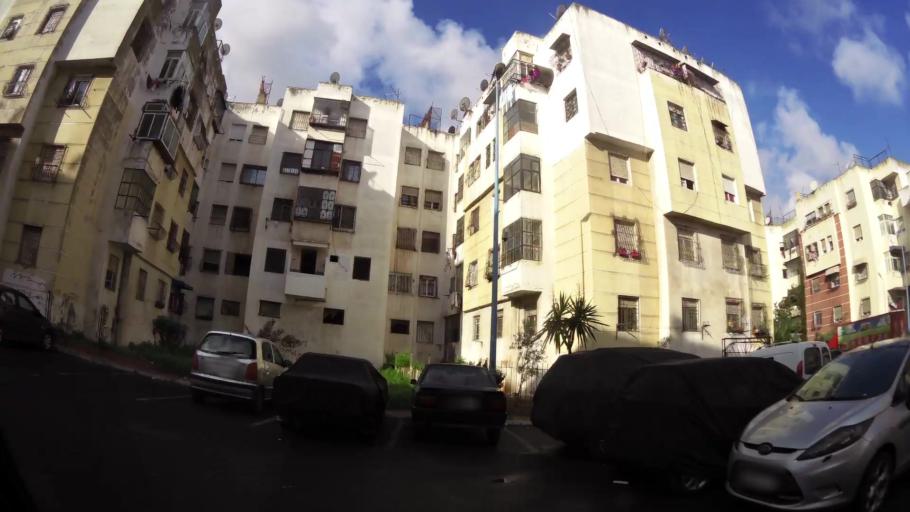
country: MA
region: Grand Casablanca
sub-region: Mediouna
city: Tit Mellil
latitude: 33.6000
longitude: -7.5342
